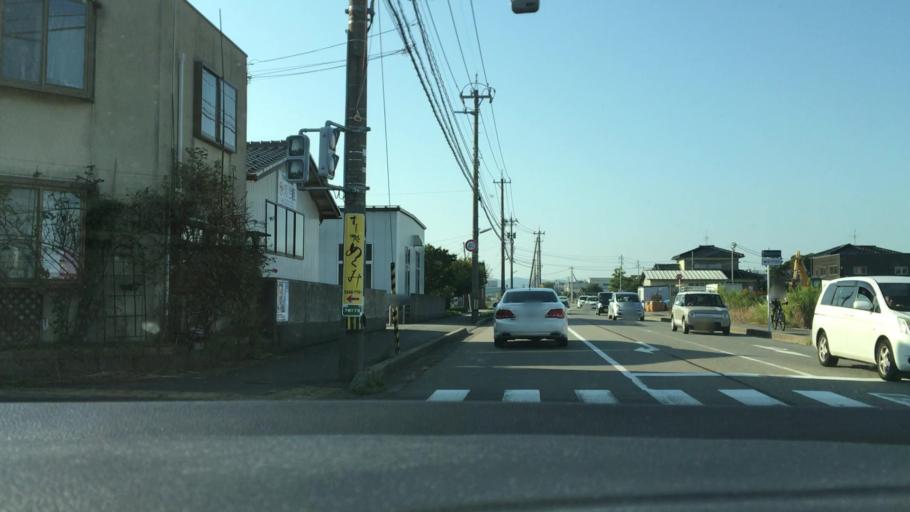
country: JP
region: Ishikawa
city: Nonoichi
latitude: 36.5211
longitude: 136.6000
